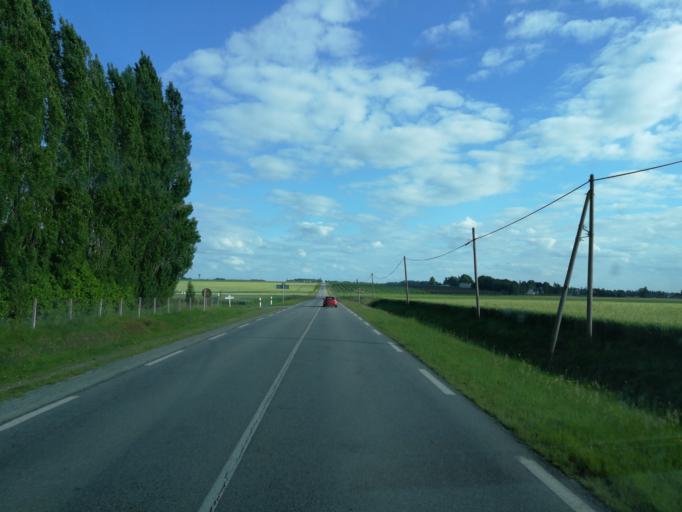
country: FR
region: Haute-Normandie
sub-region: Departement de l'Eure
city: Conches-en-Ouche
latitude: 49.0209
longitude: 0.9314
